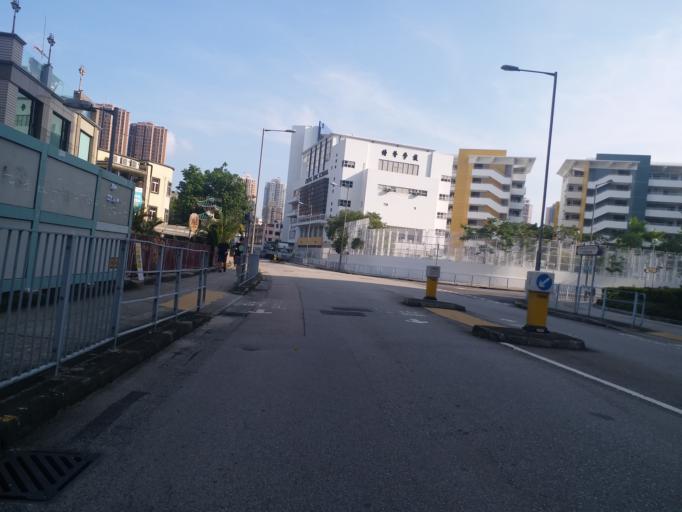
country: HK
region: Yuen Long
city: Yuen Long Kau Hui
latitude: 22.4498
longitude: 114.0334
